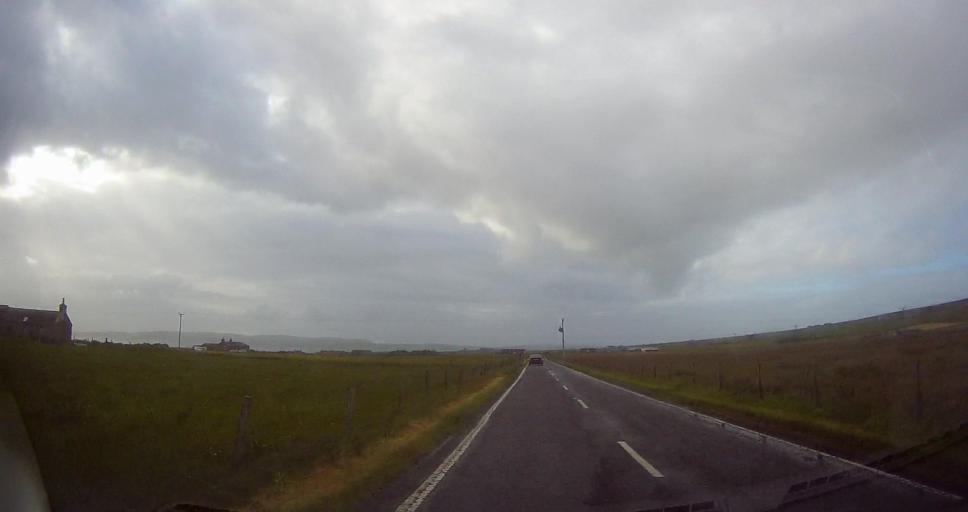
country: GB
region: Scotland
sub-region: Orkney Islands
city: Stromness
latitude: 58.9322
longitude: -3.2086
